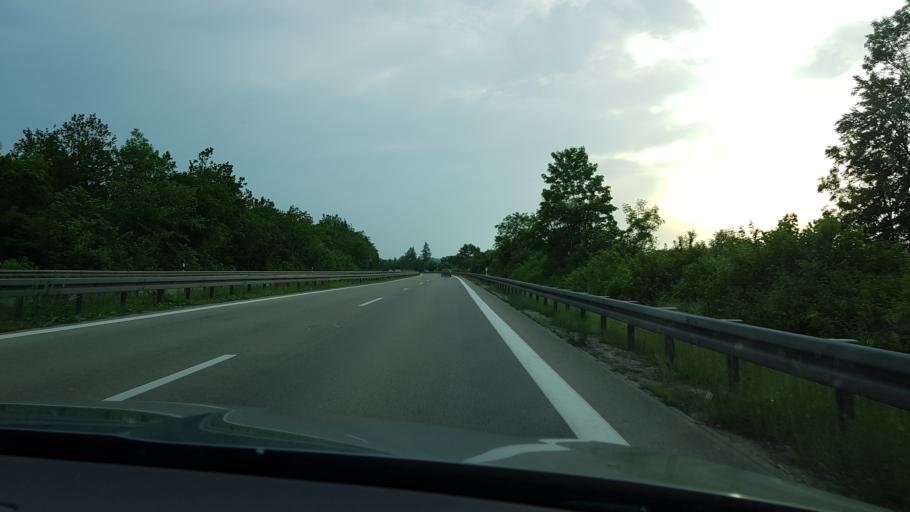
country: DE
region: Bavaria
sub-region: Upper Bavaria
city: Starnberg
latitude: 48.0040
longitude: 11.3882
